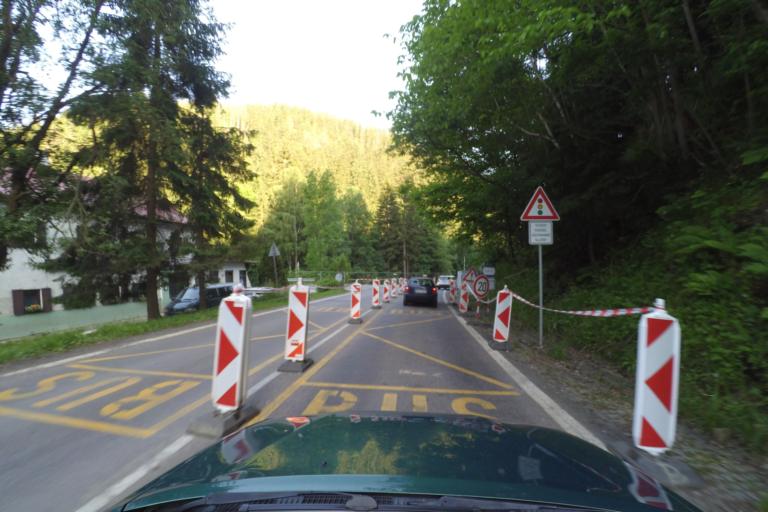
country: CZ
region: Kralovehradecky
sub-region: Okres Trutnov
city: Svoboda nad Upou
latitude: 50.6762
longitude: 15.7928
